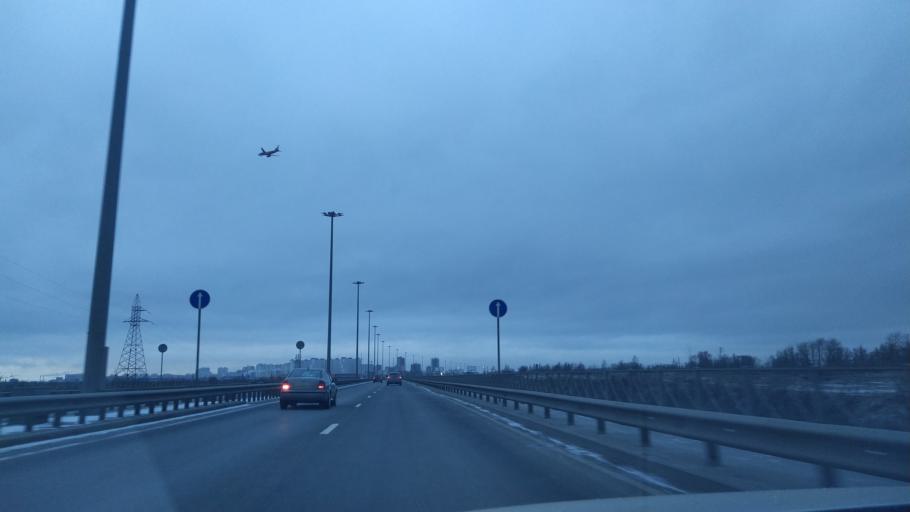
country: RU
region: St.-Petersburg
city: Shushary
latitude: 59.7816
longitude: 30.3970
